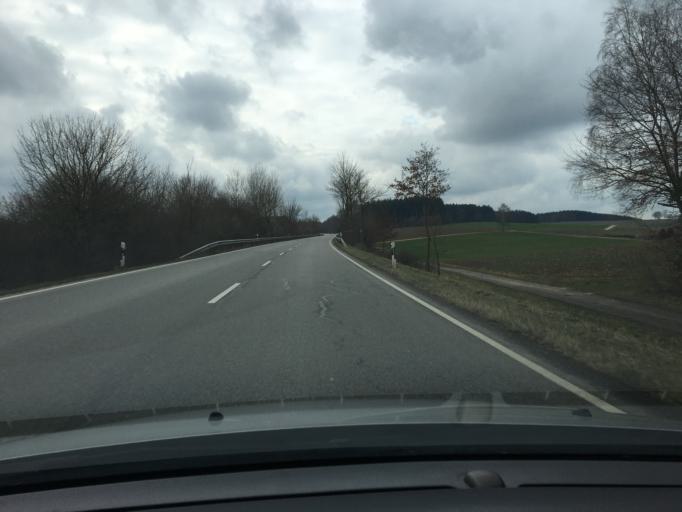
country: DE
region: Bavaria
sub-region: Lower Bavaria
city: Furth
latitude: 48.4321
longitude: 12.4021
